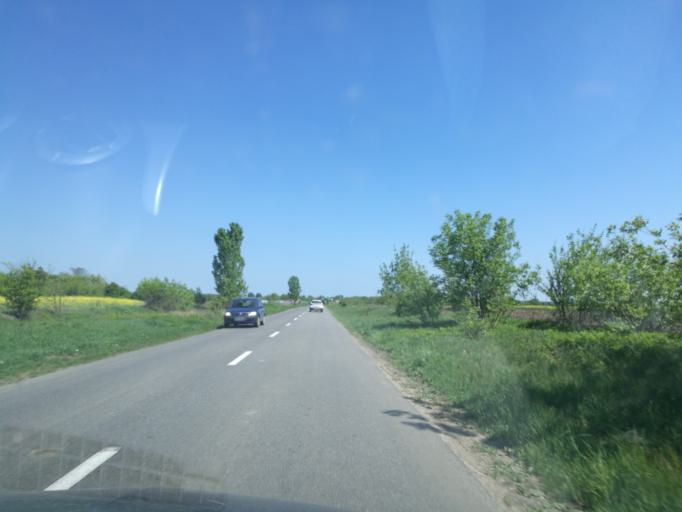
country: RO
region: Prahova
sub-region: Comuna Gherghita
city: Gherghita
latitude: 44.7905
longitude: 26.2645
